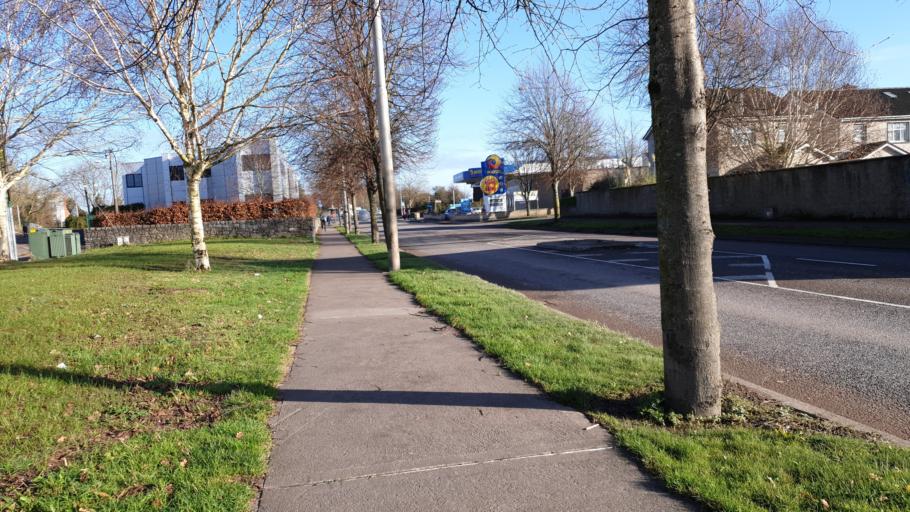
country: IE
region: Munster
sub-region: County Cork
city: Cork
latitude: 51.8899
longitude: -8.4138
